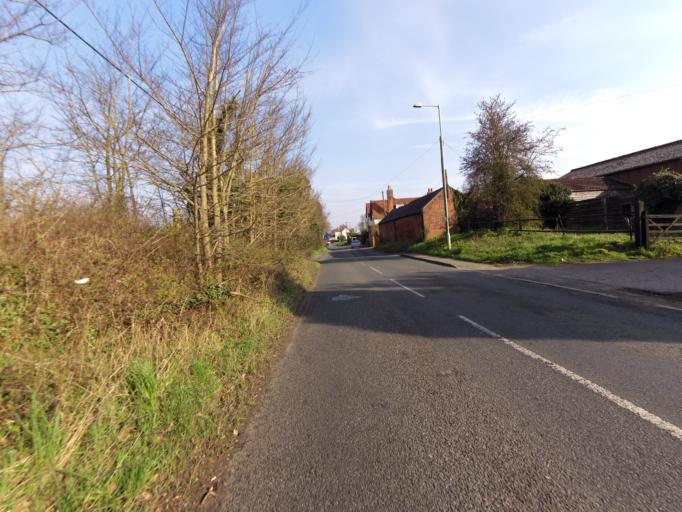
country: GB
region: England
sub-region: Suffolk
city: Bramford
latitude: 52.0754
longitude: 1.1070
